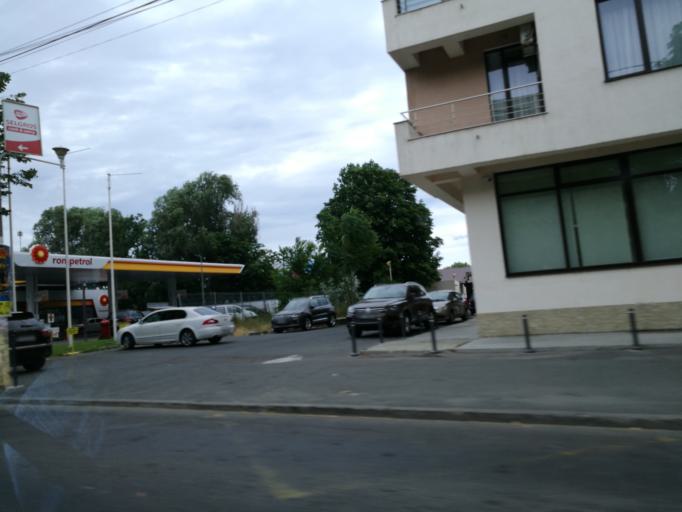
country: RO
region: Constanta
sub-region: Municipiul Constanta
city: Palazu Mare
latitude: 44.2146
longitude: 28.6284
